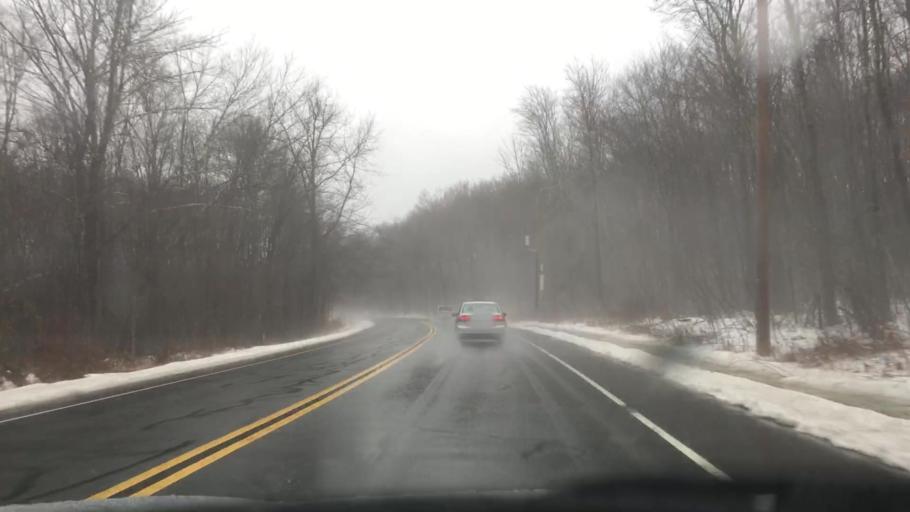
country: US
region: Massachusetts
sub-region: Hampden County
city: Ludlow
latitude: 42.2049
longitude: -72.4925
